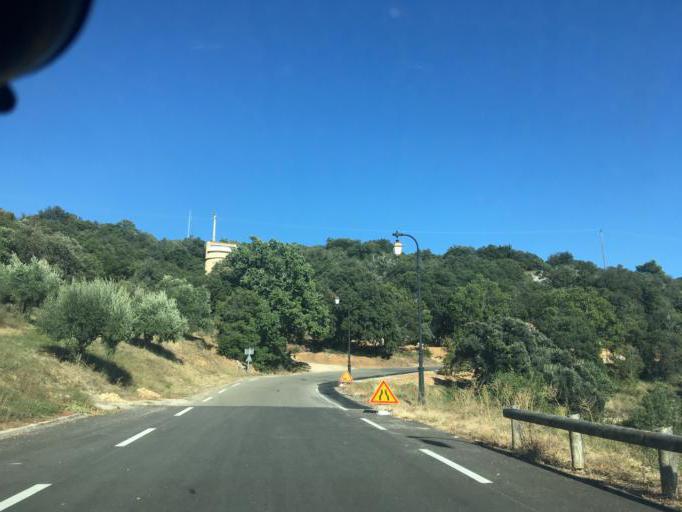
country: FR
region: Provence-Alpes-Cote d'Azur
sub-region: Departement du Var
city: Regusse
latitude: 43.7169
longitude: 6.1366
